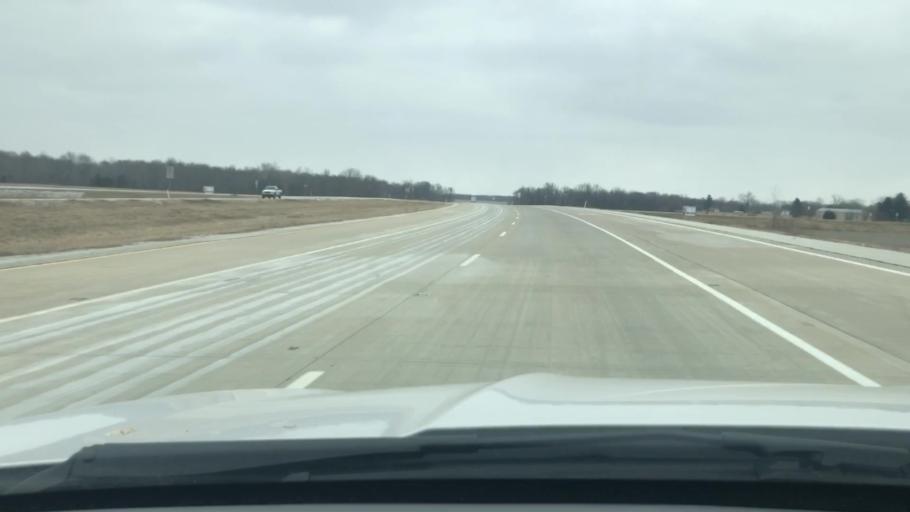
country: US
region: Indiana
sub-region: Tippecanoe County
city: Battle Ground
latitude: 40.4826
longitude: -86.7757
